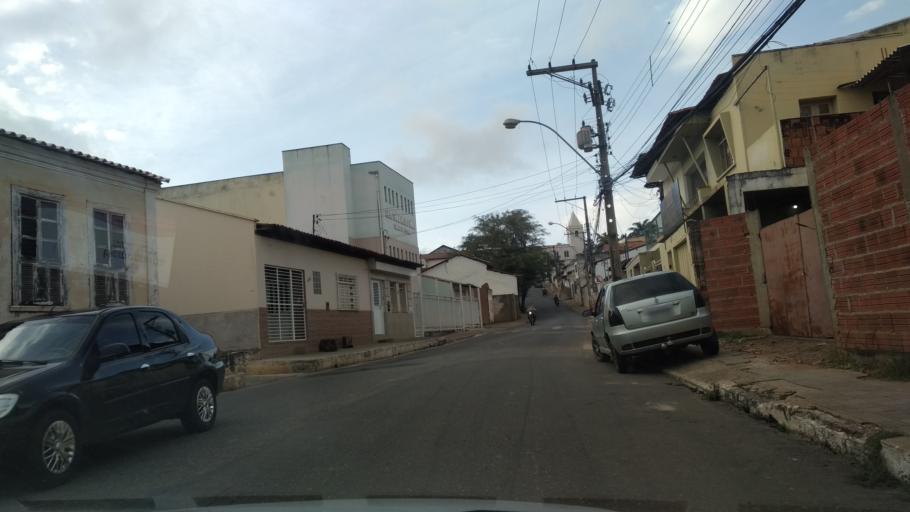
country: BR
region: Bahia
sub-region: Caetite
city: Caetite
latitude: -14.0670
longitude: -42.4845
